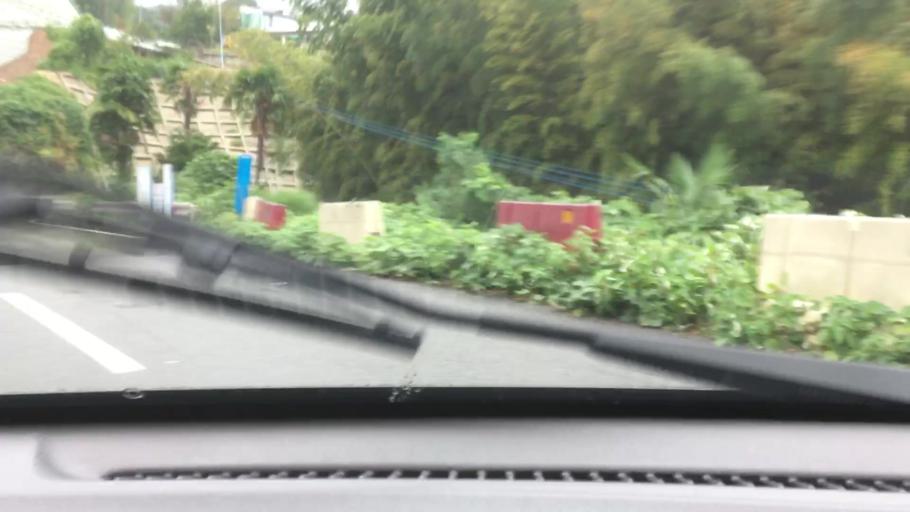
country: JP
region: Nagasaki
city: Togitsu
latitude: 32.8676
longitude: 129.7672
